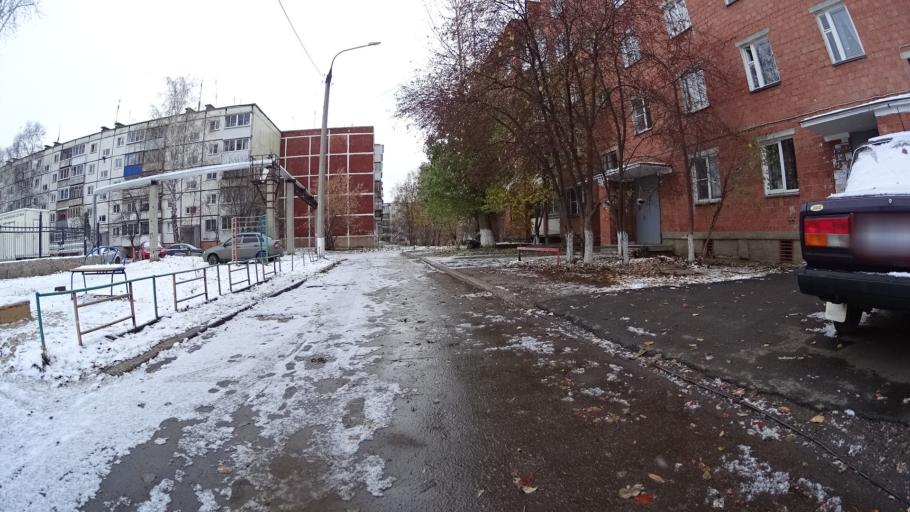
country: RU
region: Chelyabinsk
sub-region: Gorod Chelyabinsk
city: Chelyabinsk
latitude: 55.1909
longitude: 61.3092
